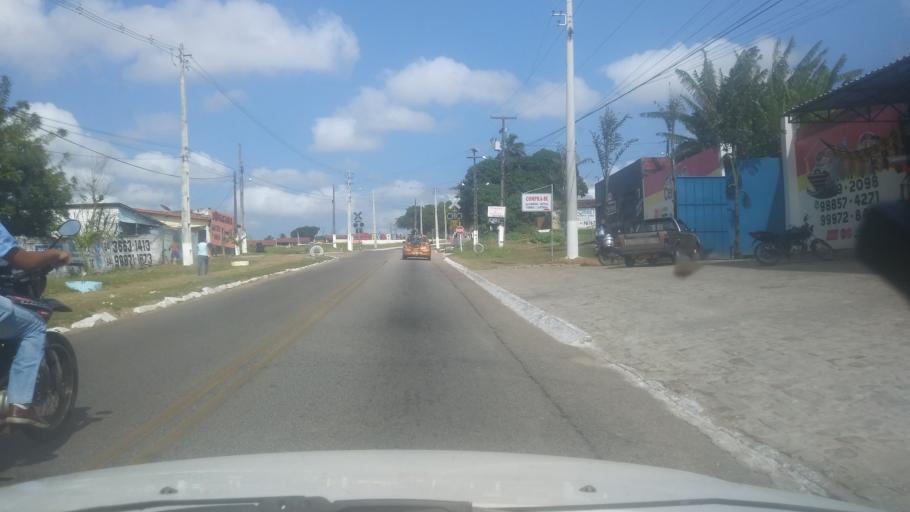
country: BR
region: Rio Grande do Norte
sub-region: Extremoz
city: Extremoz
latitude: -5.7042
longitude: -35.2847
